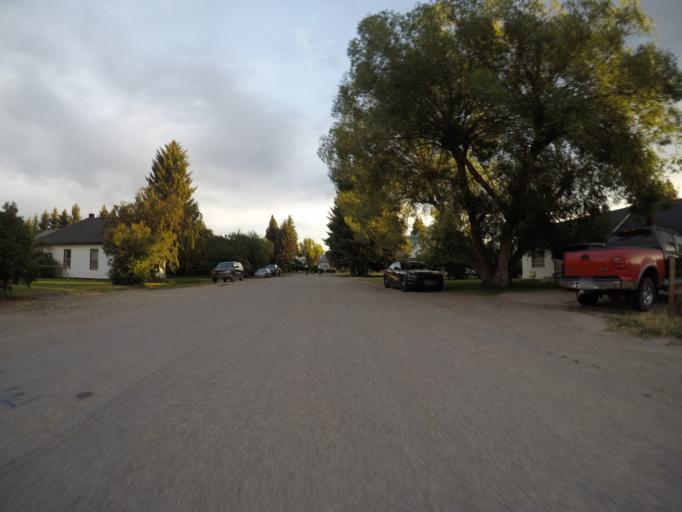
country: US
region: Idaho
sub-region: Bear Lake County
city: Montpelier
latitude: 42.0848
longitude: -110.9552
